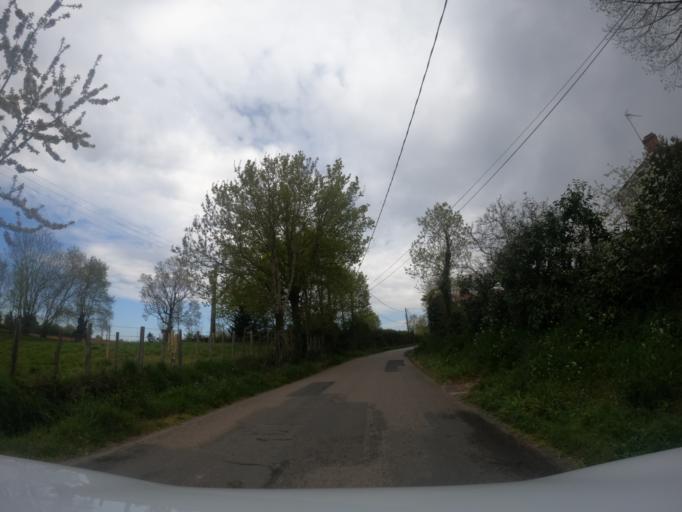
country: FR
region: Pays de la Loire
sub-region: Departement de la Vendee
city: Le Champ-Saint-Pere
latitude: 46.5304
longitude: -1.3303
